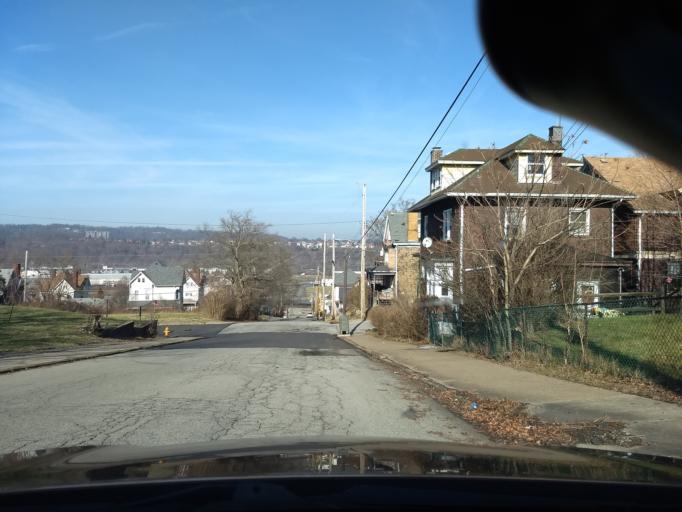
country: US
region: Pennsylvania
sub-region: Allegheny County
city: Homestead
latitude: 40.4065
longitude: -79.8995
